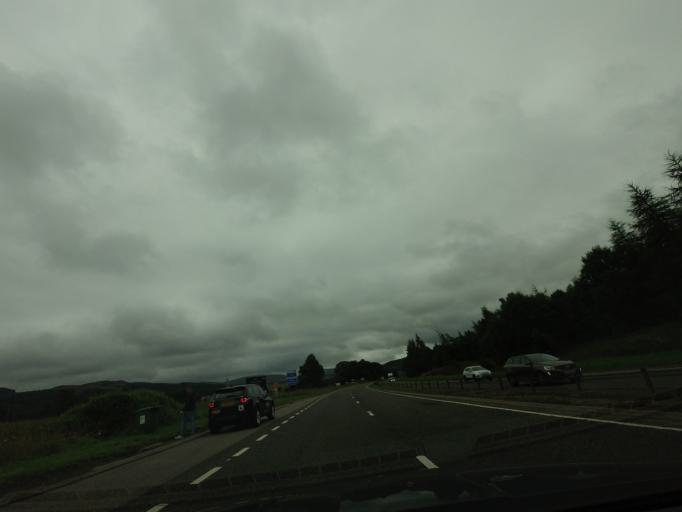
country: GB
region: Scotland
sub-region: Highland
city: Inverness
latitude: 57.4340
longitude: -4.1322
